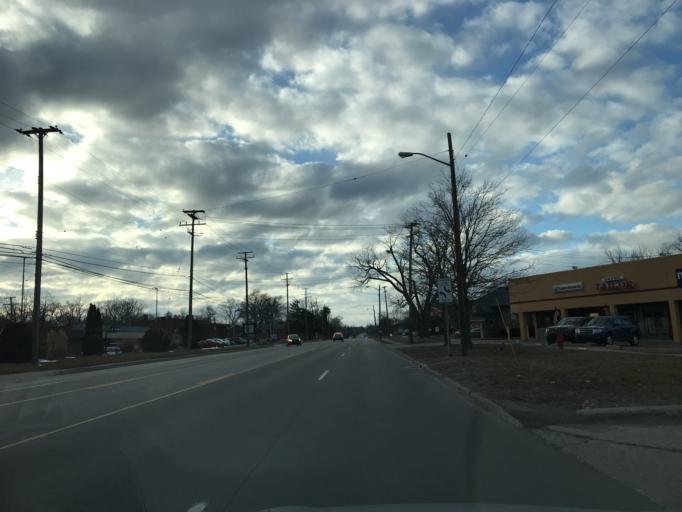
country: US
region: Michigan
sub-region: Oakland County
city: Farmington
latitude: 42.4571
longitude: -83.3582
